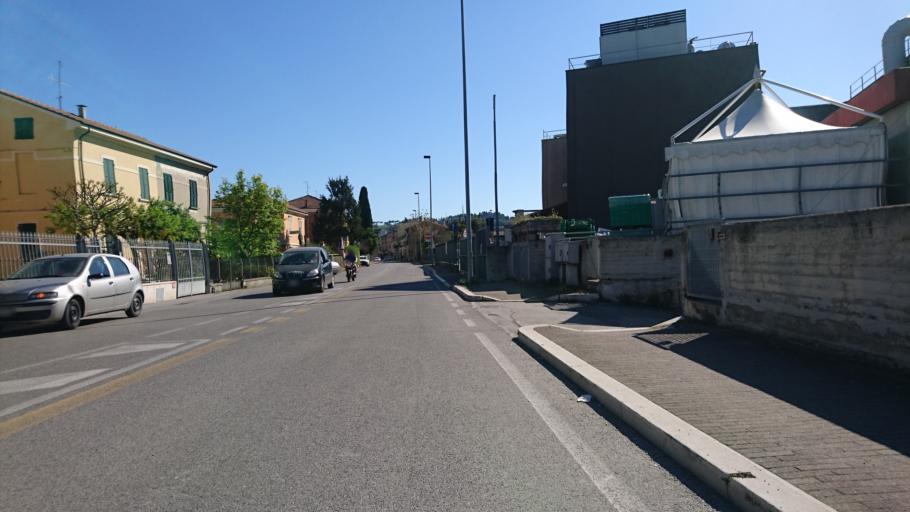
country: IT
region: The Marches
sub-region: Provincia di Pesaro e Urbino
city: Pesaro
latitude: 43.9007
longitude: 12.9023
